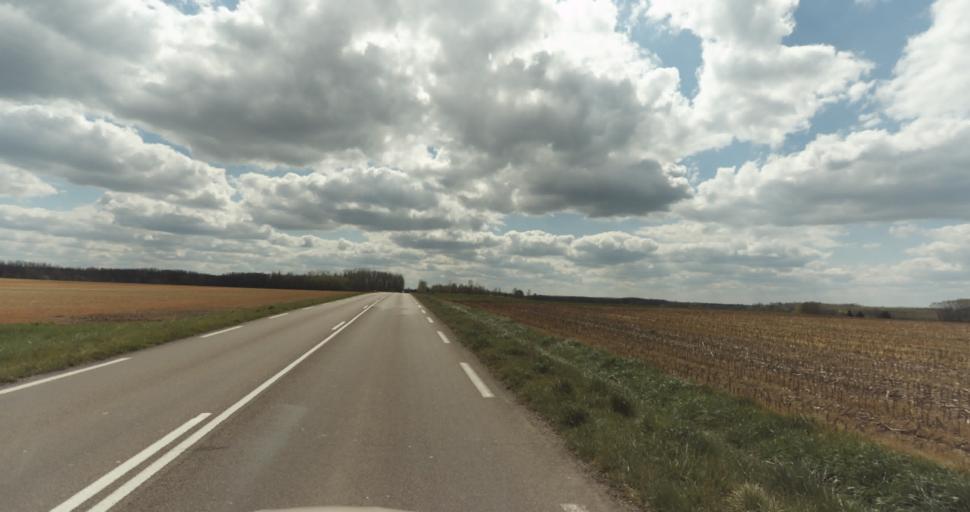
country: FR
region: Bourgogne
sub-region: Departement de la Cote-d'Or
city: Auxonne
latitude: 47.1742
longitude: 5.4019
